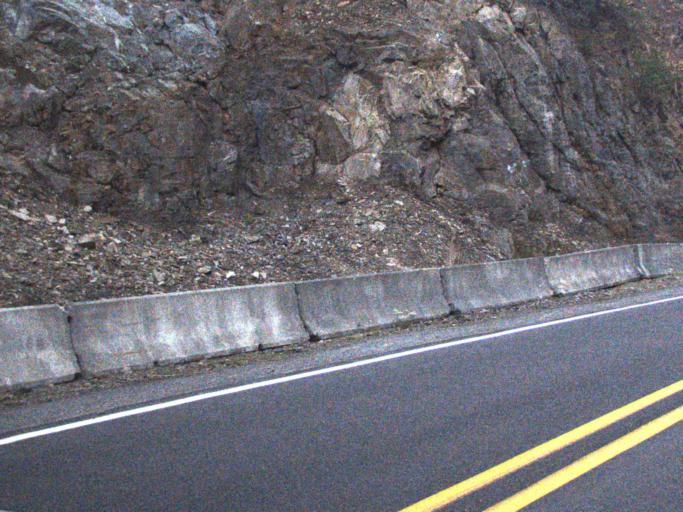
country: US
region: Washington
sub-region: Snohomish County
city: Darrington
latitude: 48.6927
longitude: -120.8941
